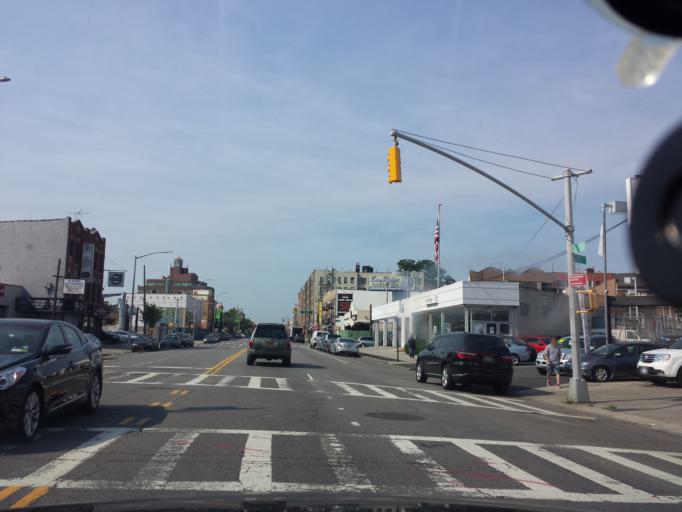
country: US
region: New York
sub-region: Kings County
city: Bensonhurst
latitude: 40.6206
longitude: -74.0293
